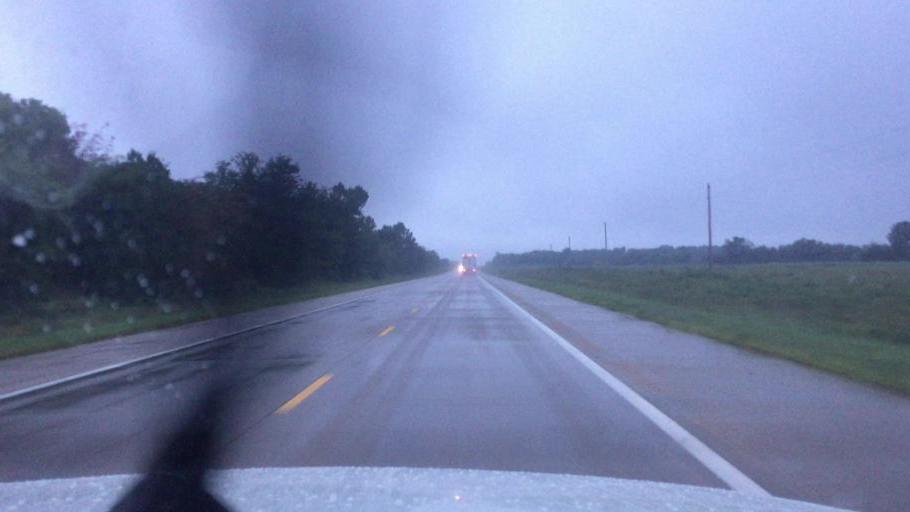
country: US
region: Kansas
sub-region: Neosho County
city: Chanute
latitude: 37.5544
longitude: -95.4709
